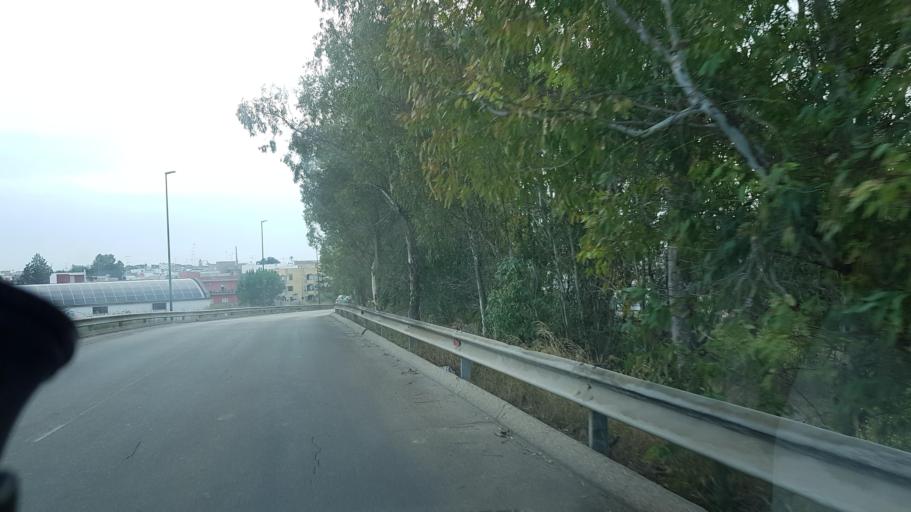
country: IT
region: Apulia
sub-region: Provincia di Lecce
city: Trepuzzi
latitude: 40.4125
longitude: 18.0736
